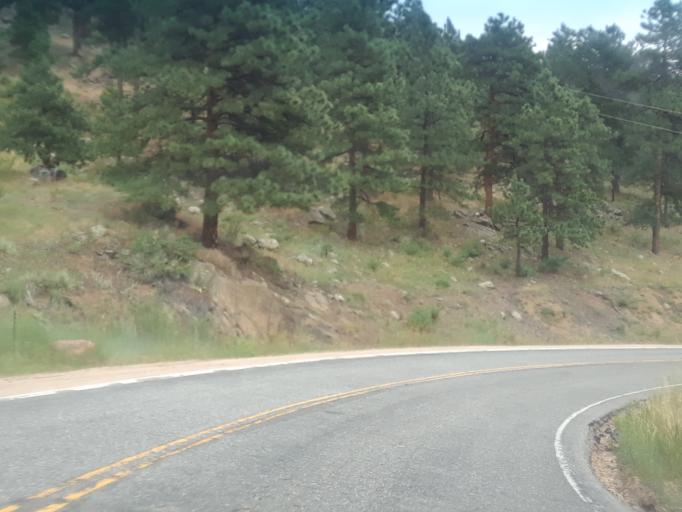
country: US
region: Colorado
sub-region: Boulder County
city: Boulder
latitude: 40.0329
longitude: -105.3198
